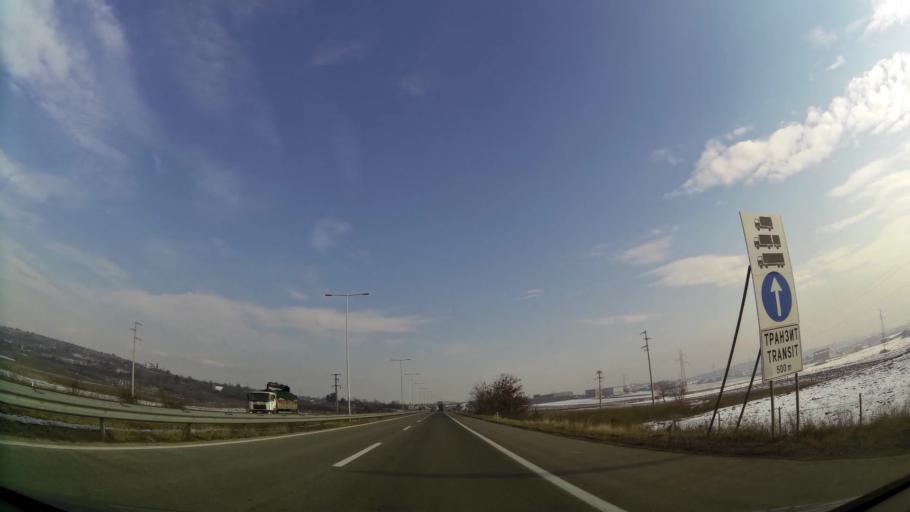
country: MK
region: Suto Orizari
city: Suto Orizare
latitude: 42.0531
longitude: 21.4115
